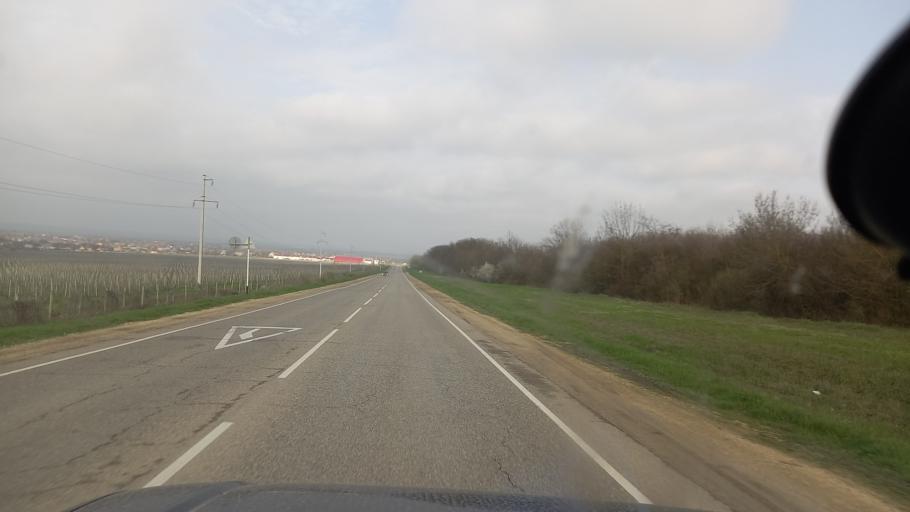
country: RU
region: Krasnodarskiy
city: Varenikovskaya
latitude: 45.1064
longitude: 37.6162
